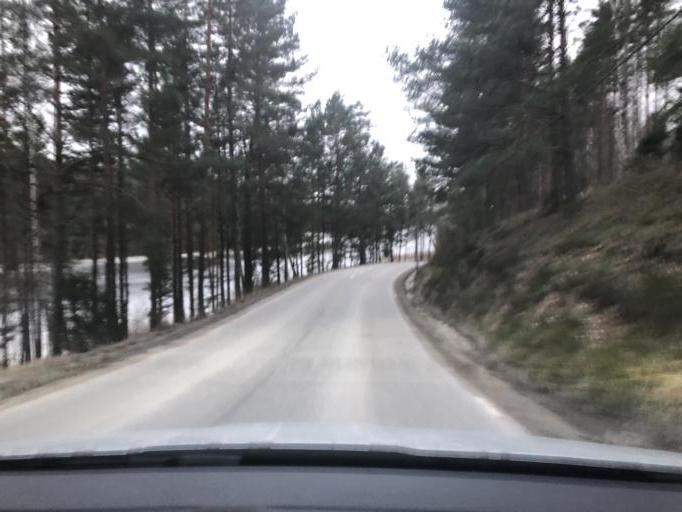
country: SE
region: Stockholm
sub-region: Botkyrka Kommun
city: Tullinge
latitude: 59.1627
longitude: 17.8941
